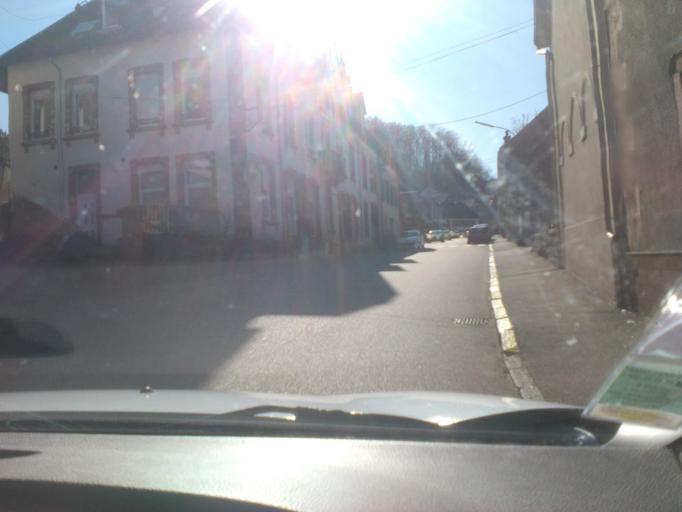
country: FR
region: Alsace
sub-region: Departement du Bas-Rhin
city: Rothau
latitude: 48.4554
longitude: 7.2073
